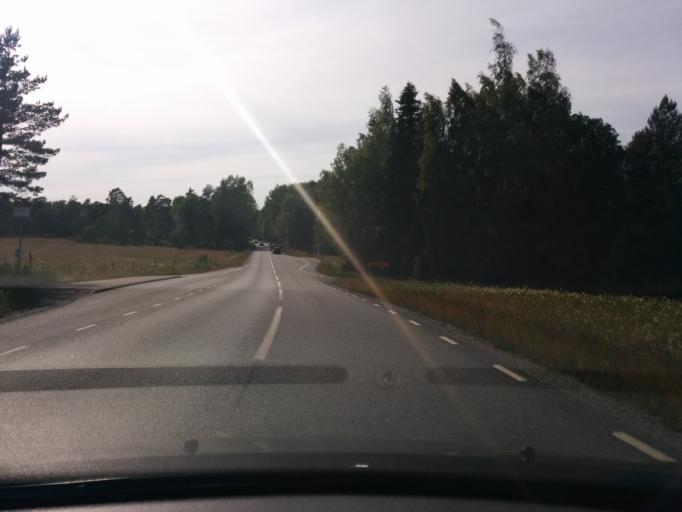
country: SE
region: Stockholm
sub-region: Varmdo Kommun
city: Holo
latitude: 59.2814
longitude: 18.6214
